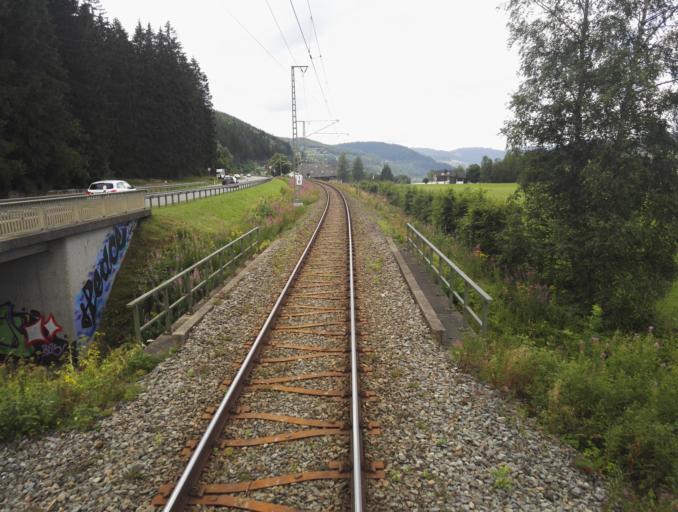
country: DE
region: Baden-Wuerttemberg
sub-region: Freiburg Region
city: Titisee-Neustadt
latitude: 47.8993
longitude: 8.1613
